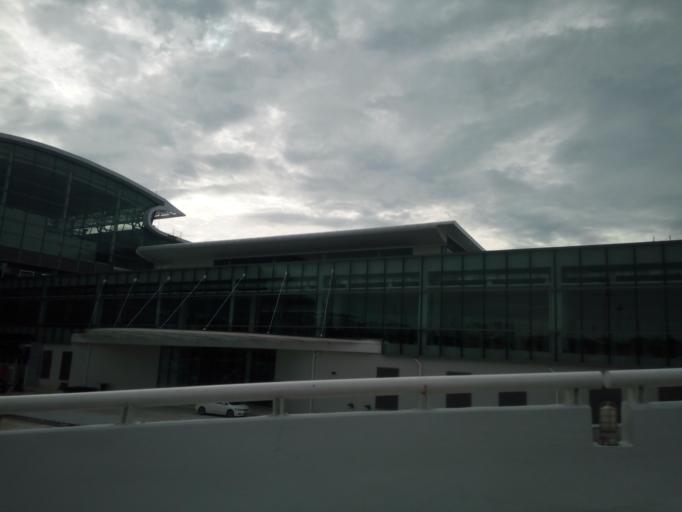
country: TH
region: Phuket
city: Thalang
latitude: 8.1068
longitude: 98.3063
